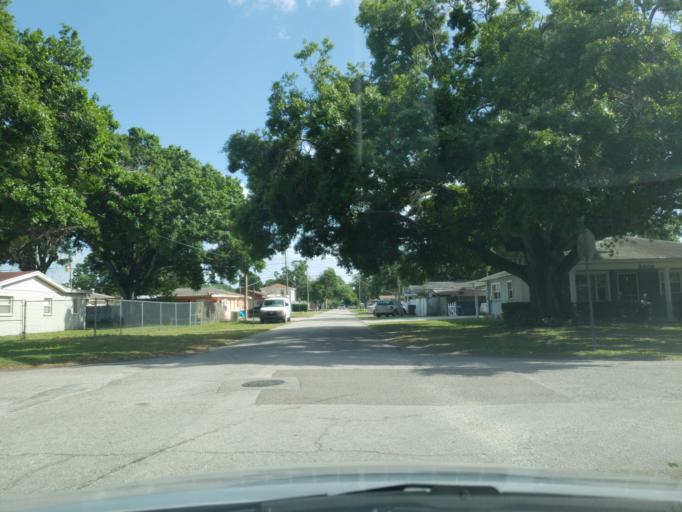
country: US
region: Florida
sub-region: Hillsborough County
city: Egypt Lake-Leto
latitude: 27.9734
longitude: -82.4993
